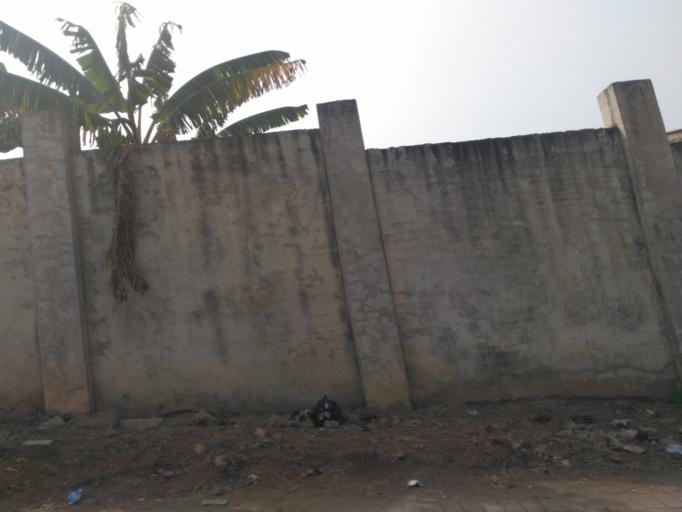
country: GH
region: Ashanti
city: Kumasi
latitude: 6.6682
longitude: -1.6079
